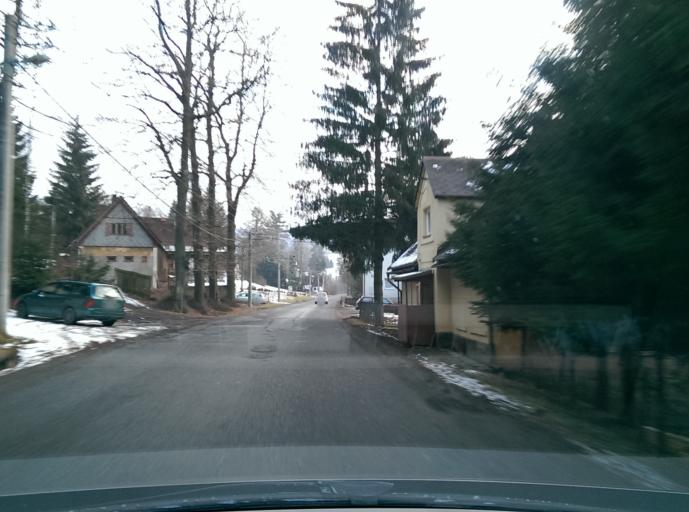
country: CZ
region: Liberecky
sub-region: Okres Jablonec nad Nisou
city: Smrzovka
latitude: 50.7465
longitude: 15.2662
